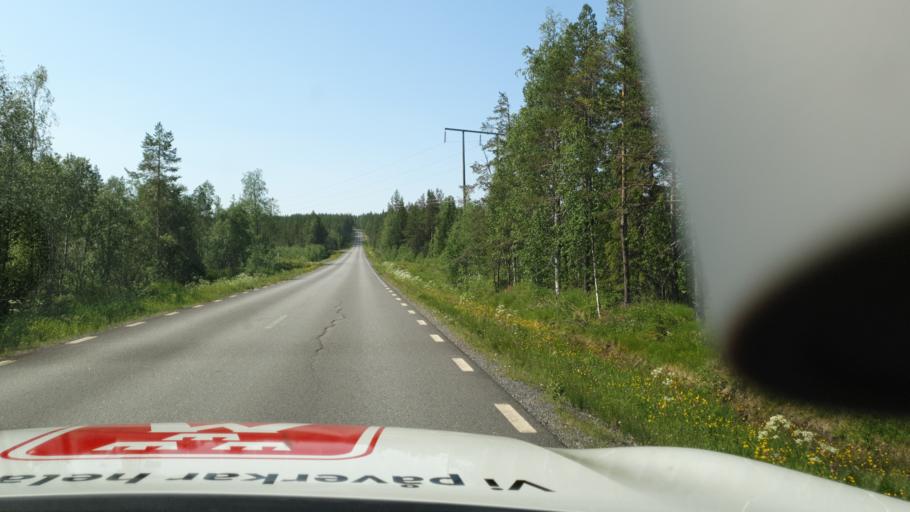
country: SE
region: Vaesterbotten
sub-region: Skelleftea Kommun
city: Langsele
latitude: 64.9810
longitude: 20.0655
